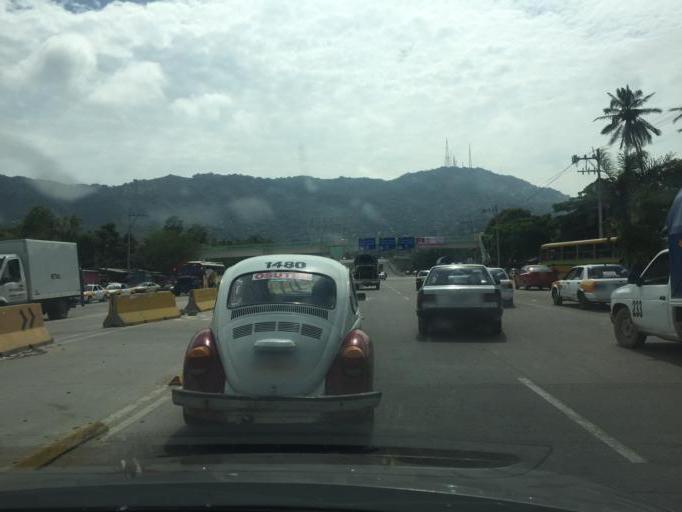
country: MX
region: Guerrero
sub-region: Acapulco de Juarez
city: Colonia Alborada
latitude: 16.8903
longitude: -99.8359
